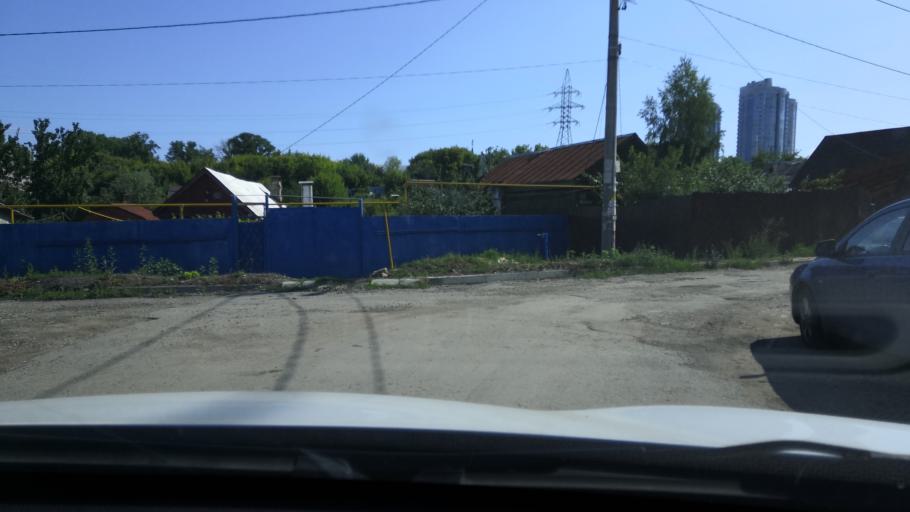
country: RU
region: Samara
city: Samara
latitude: 53.2213
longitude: 50.1603
